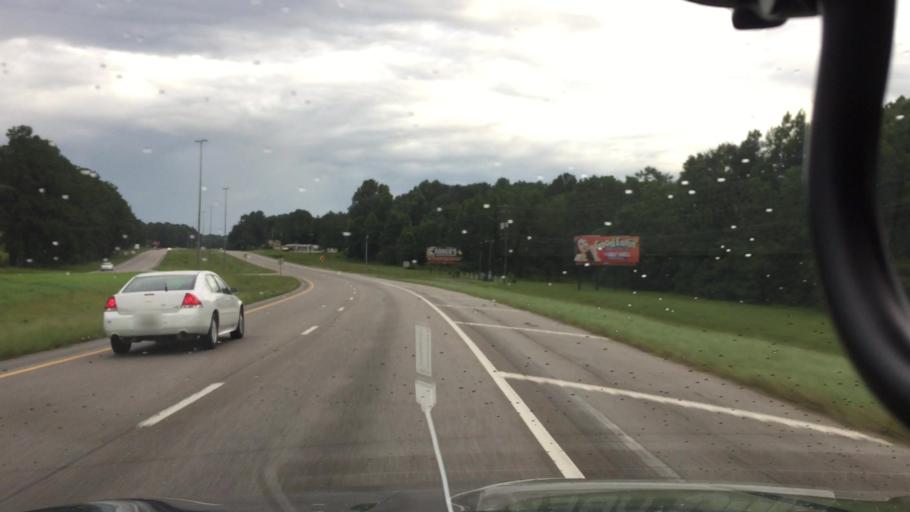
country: US
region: Alabama
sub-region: Pike County
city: Troy
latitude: 31.8430
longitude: -85.9948
